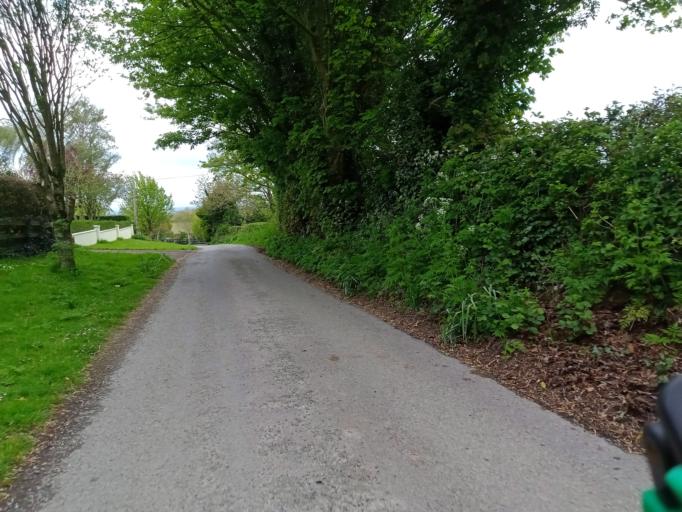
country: IE
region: Leinster
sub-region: Kilkenny
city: Kilkenny
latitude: 52.6229
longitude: -7.2387
